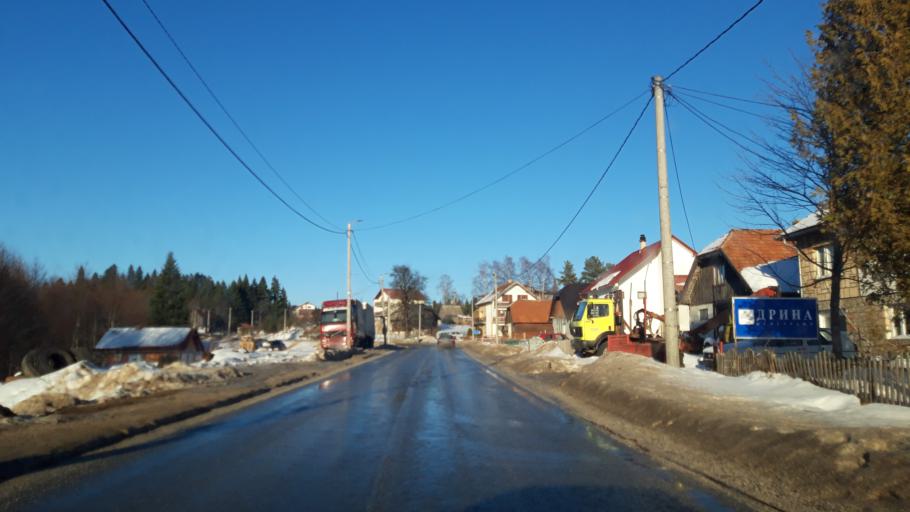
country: BA
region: Republika Srpska
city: Han Pijesak
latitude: 44.0714
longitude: 18.9470
